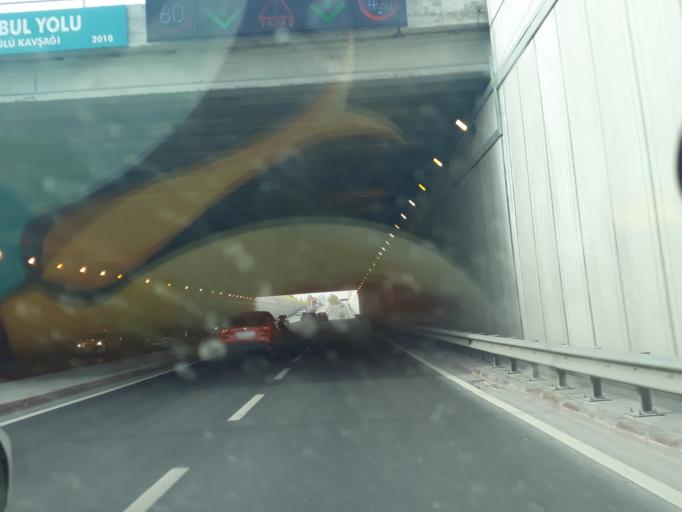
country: TR
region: Konya
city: Selcuklu
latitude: 37.9591
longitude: 32.5141
